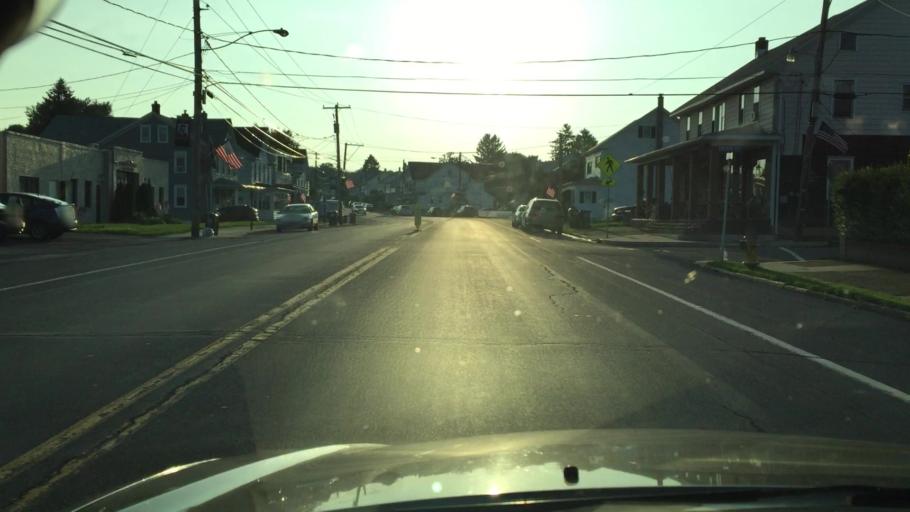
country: US
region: Pennsylvania
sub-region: Luzerne County
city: Oakdale
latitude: 40.9282
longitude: -75.9101
